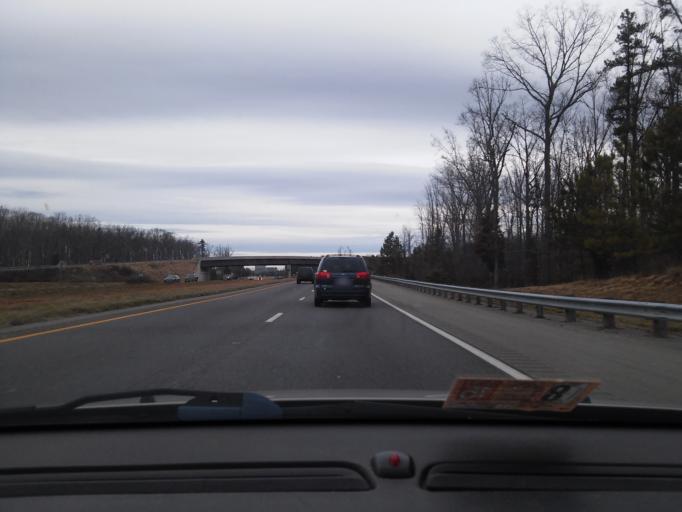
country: US
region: Virginia
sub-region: Henrico County
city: Short Pump
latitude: 37.6348
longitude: -77.6636
